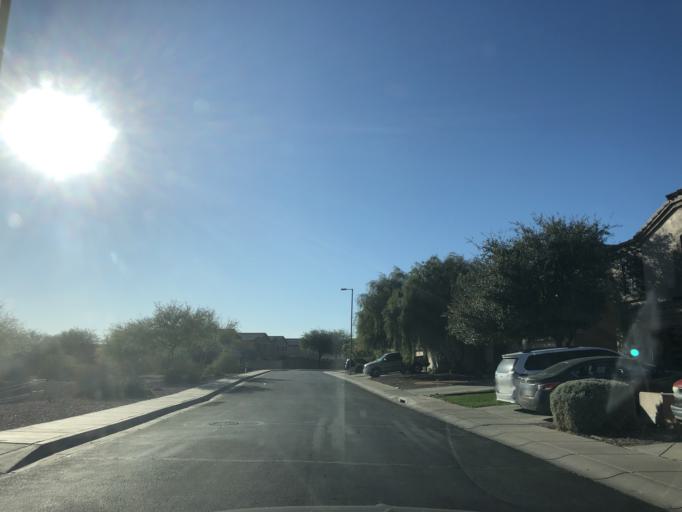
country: US
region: Arizona
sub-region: Maricopa County
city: Buckeye
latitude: 33.4395
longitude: -112.5682
